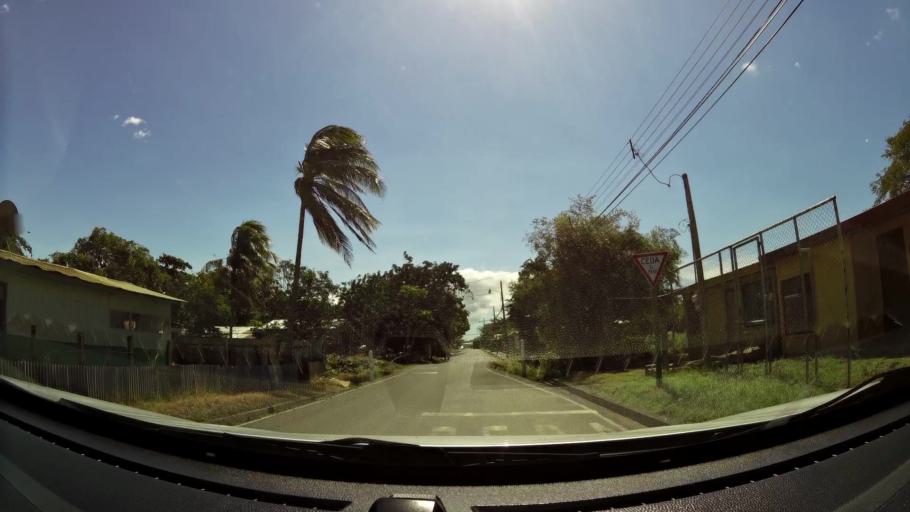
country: CR
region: Guanacaste
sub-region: Canton de Canas
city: Canas
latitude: 10.4274
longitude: -85.1018
